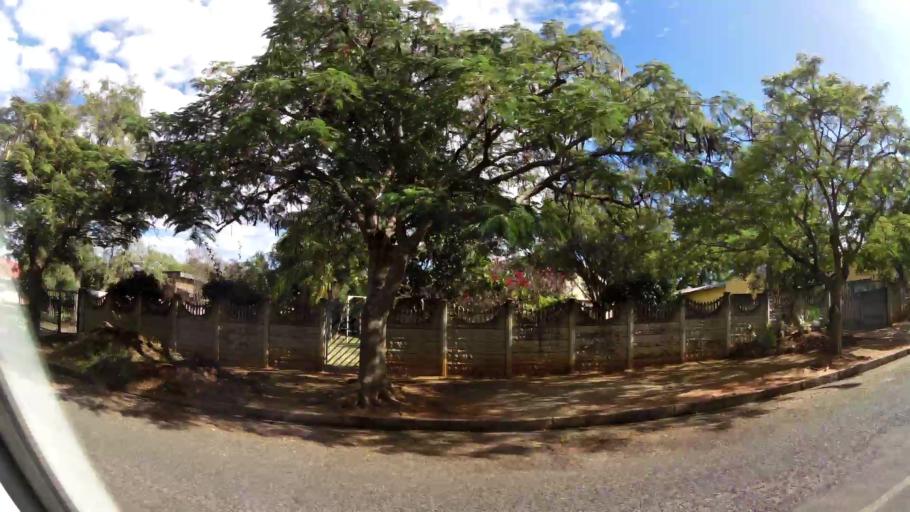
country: ZA
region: Limpopo
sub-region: Waterberg District Municipality
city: Warmbaths
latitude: -24.8767
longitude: 28.2884
